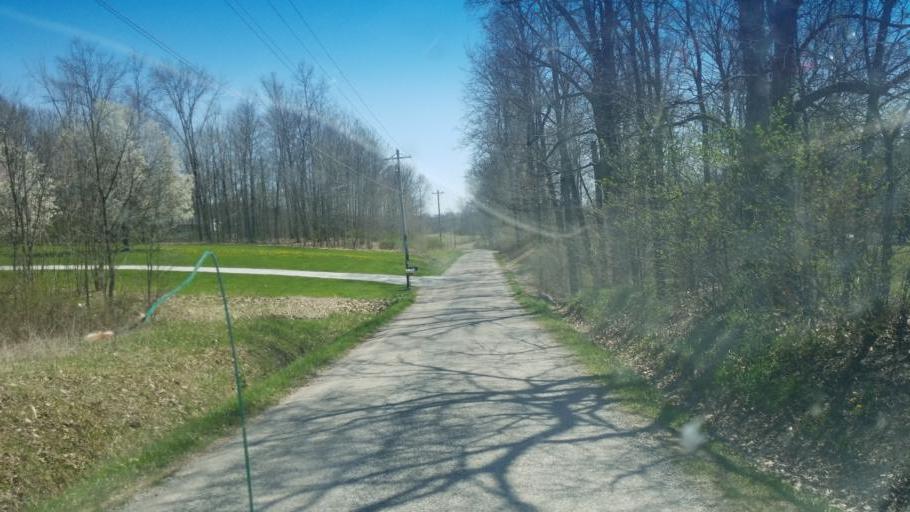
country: US
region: Ohio
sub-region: Ashland County
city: Ashland
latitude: 40.8457
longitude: -82.3877
